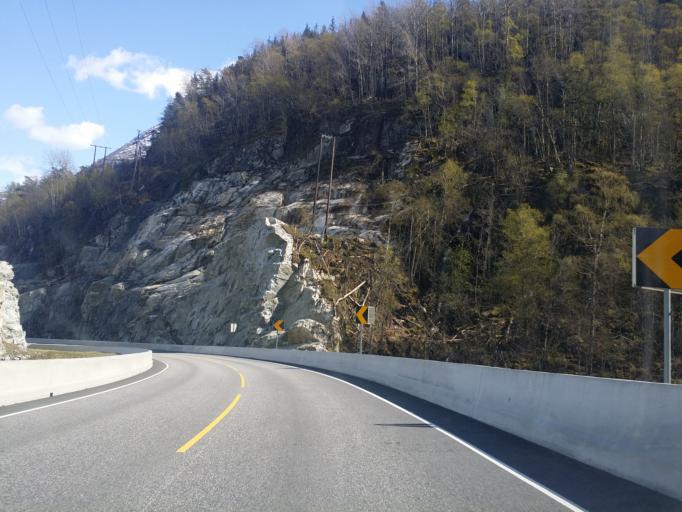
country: NO
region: Hordaland
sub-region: Ulvik
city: Ulvik
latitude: 60.4681
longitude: 6.8714
